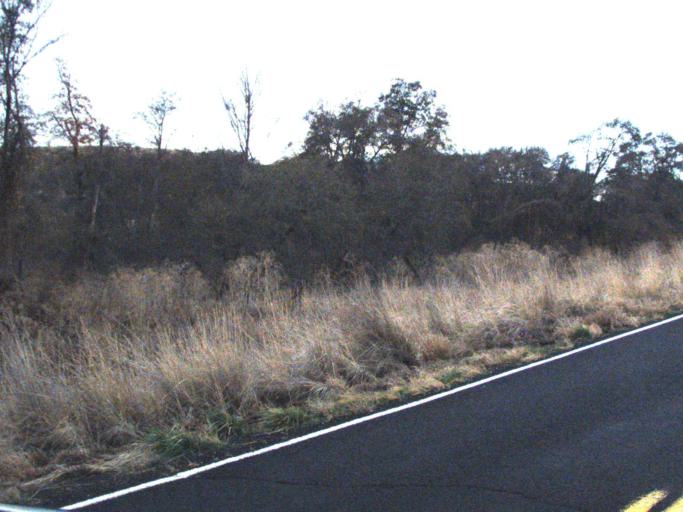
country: US
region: Washington
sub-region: Columbia County
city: Dayton
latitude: 46.5058
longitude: -118.0439
